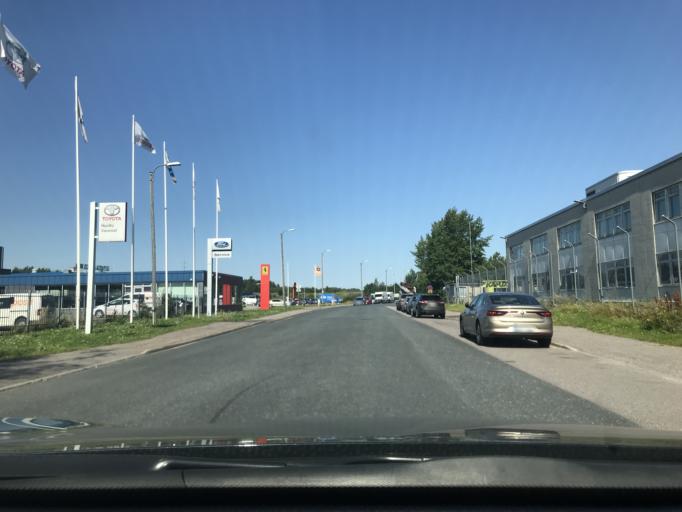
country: FI
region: Uusimaa
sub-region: Helsinki
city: Vantaa
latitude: 60.2436
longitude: 25.0464
